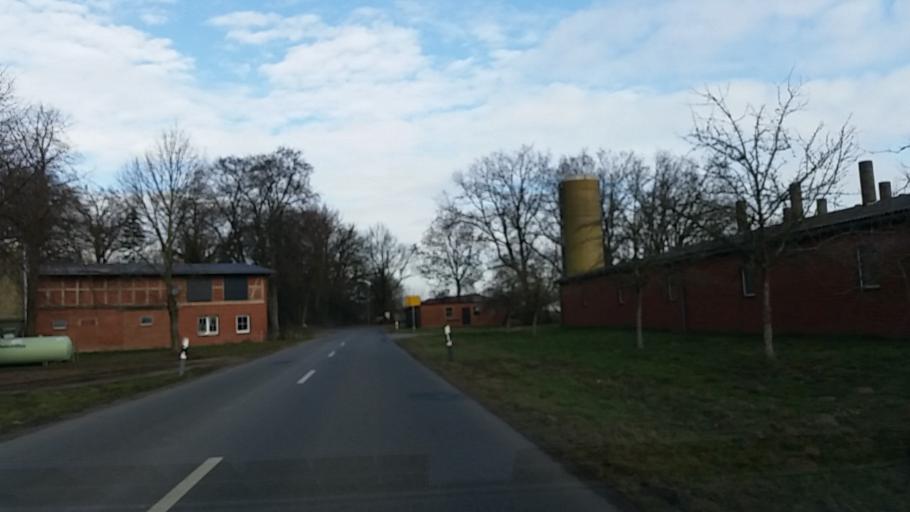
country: DE
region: Lower Saxony
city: Altenmedingen
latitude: 53.1343
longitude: 10.6362
